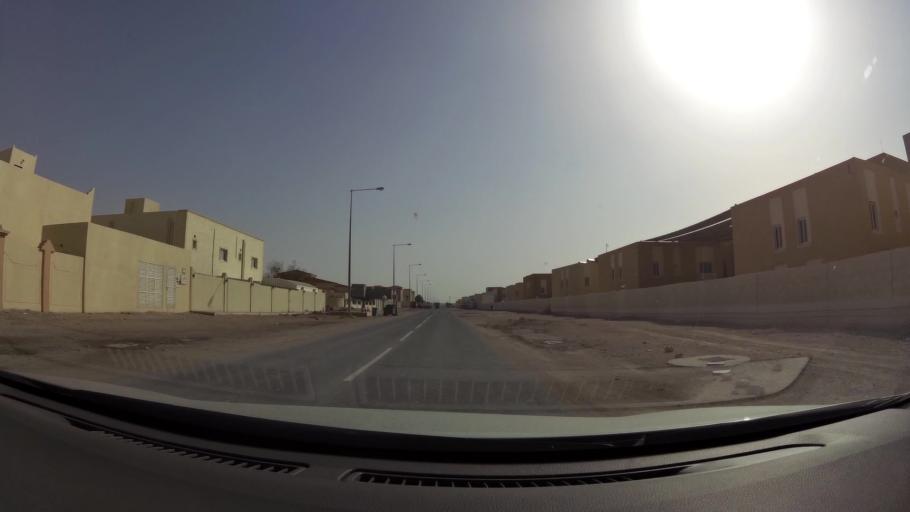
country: QA
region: Baladiyat ar Rayyan
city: Ar Rayyan
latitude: 25.3340
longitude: 51.4214
